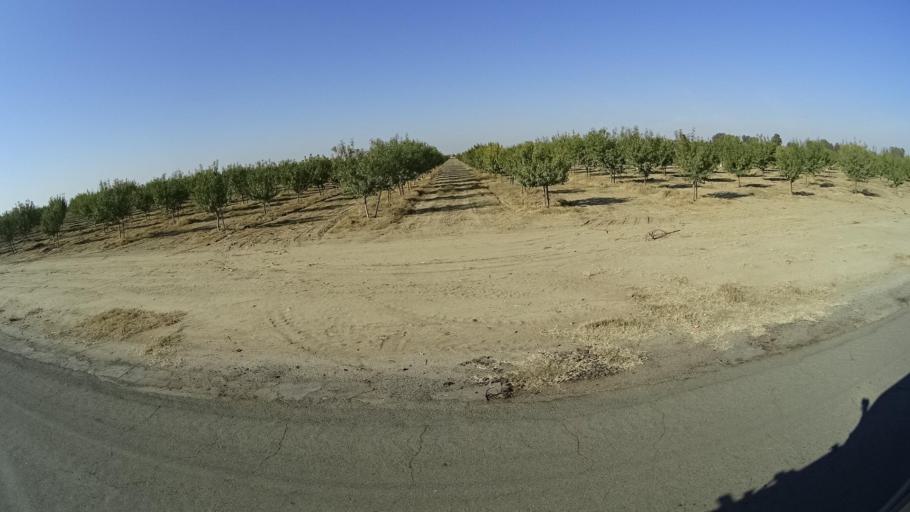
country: US
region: California
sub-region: Kern County
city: Delano
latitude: 35.7516
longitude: -119.2319
